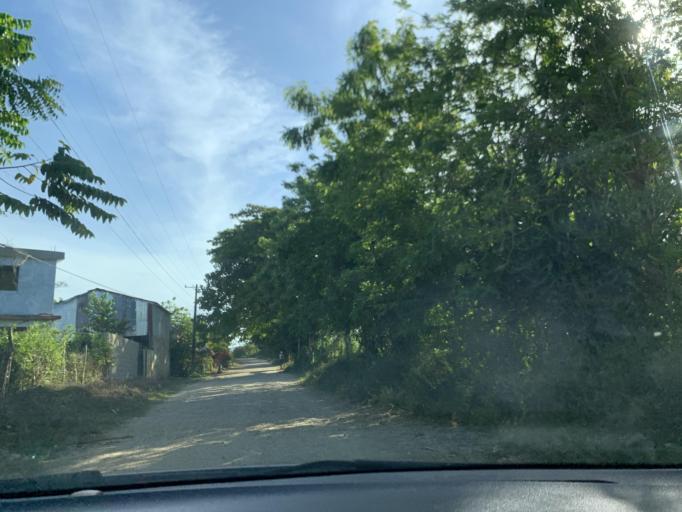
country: DO
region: Puerto Plata
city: Luperon
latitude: 19.8703
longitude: -70.9414
